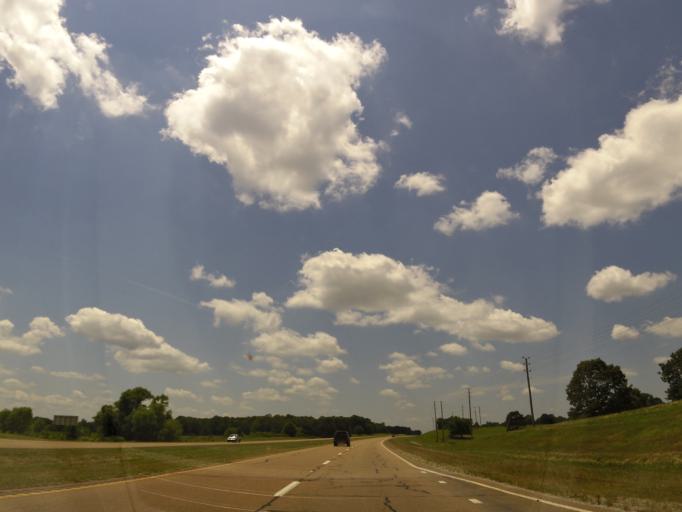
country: US
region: Mississippi
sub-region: Pontotoc County
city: Pontotoc
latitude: 34.2820
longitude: -89.0594
